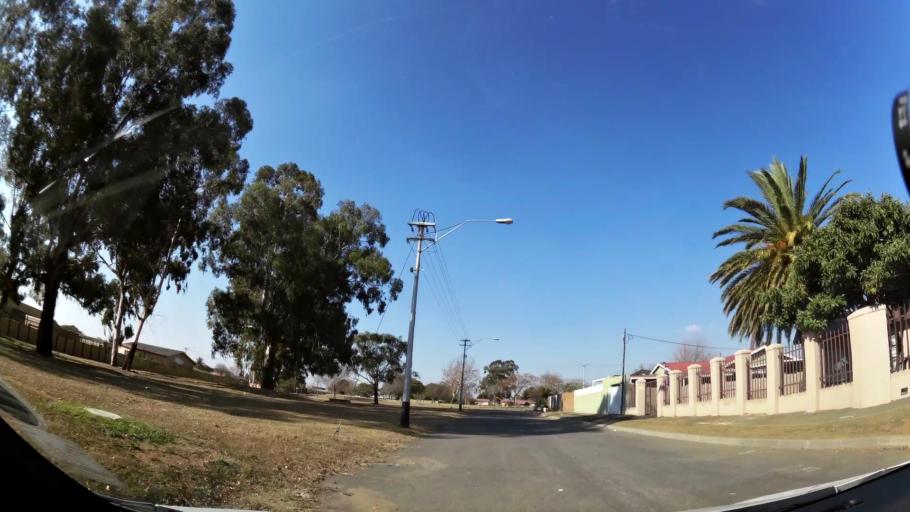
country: ZA
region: Gauteng
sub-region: City of Johannesburg Metropolitan Municipality
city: Johannesburg
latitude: -26.2536
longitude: 28.0035
